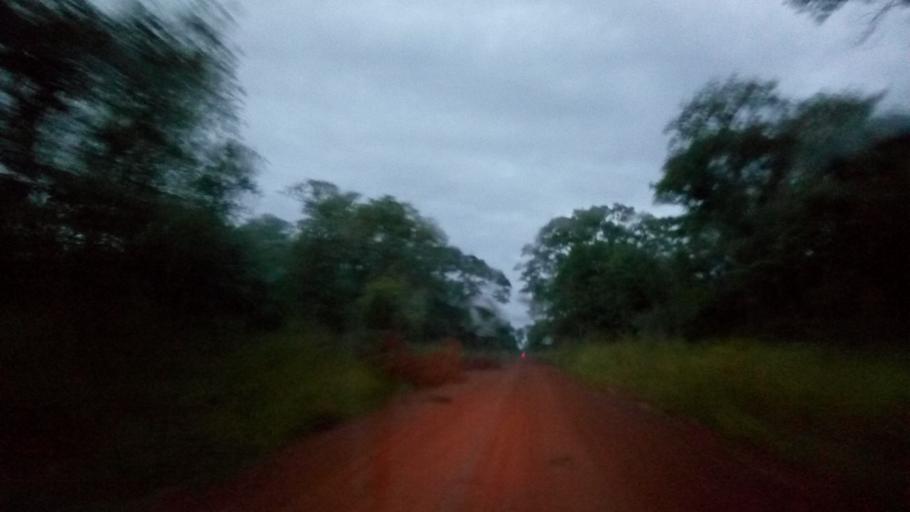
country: ZM
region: Luapula
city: Nchelenge
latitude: -9.8133
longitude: 28.1401
